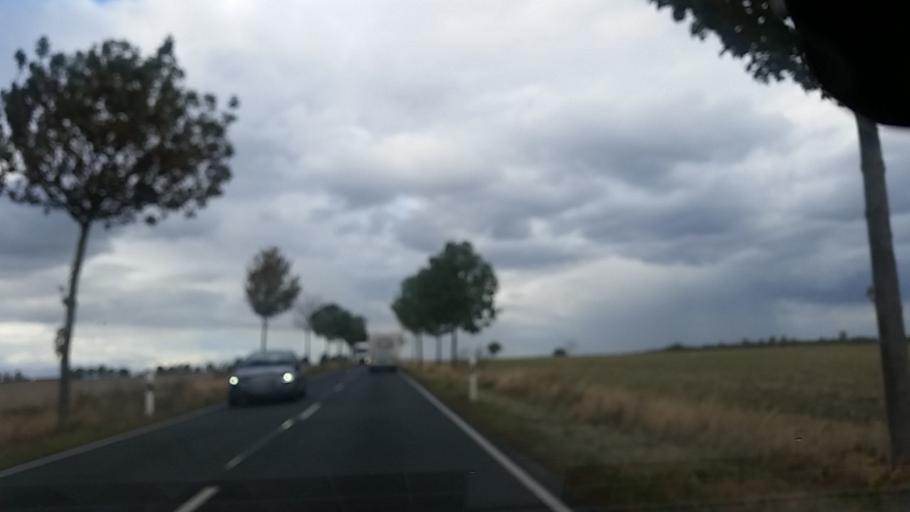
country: DE
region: Lower Saxony
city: Danndorf
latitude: 52.4000
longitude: 10.8497
